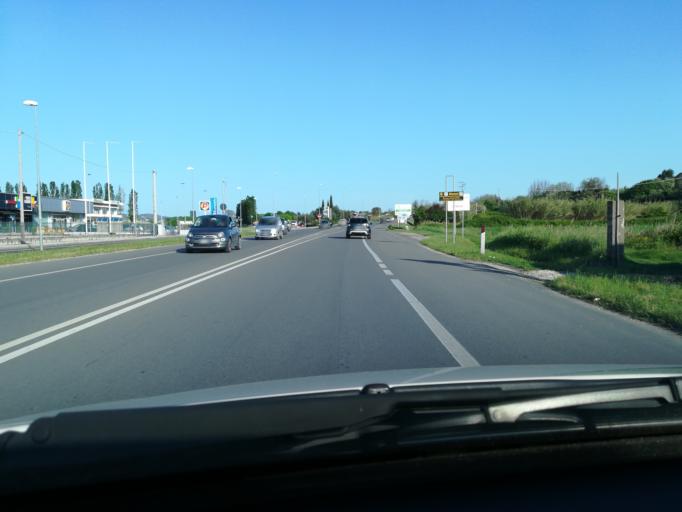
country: IT
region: Emilia-Romagna
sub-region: Provincia di Rimini
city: Misano Adriatico
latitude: 43.9695
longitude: 12.7058
